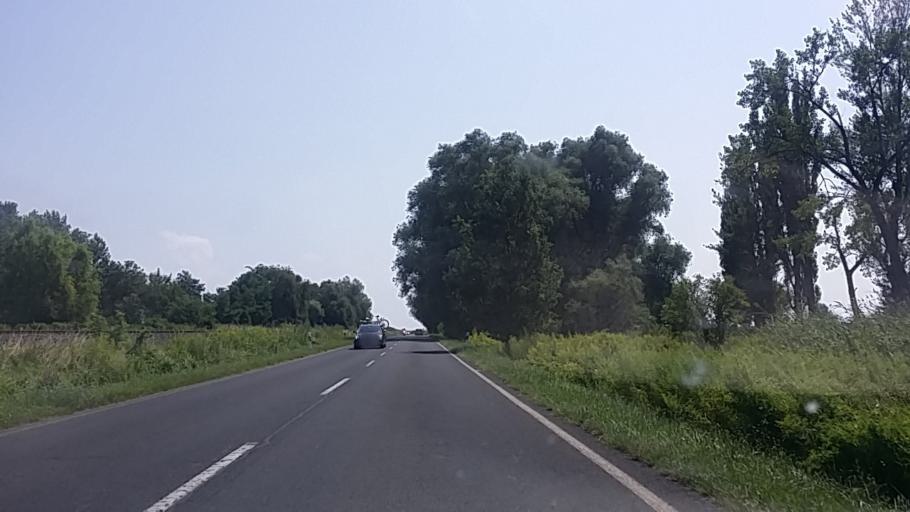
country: HU
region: Veszprem
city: Badacsonytomaj
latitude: 46.7982
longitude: 17.4694
